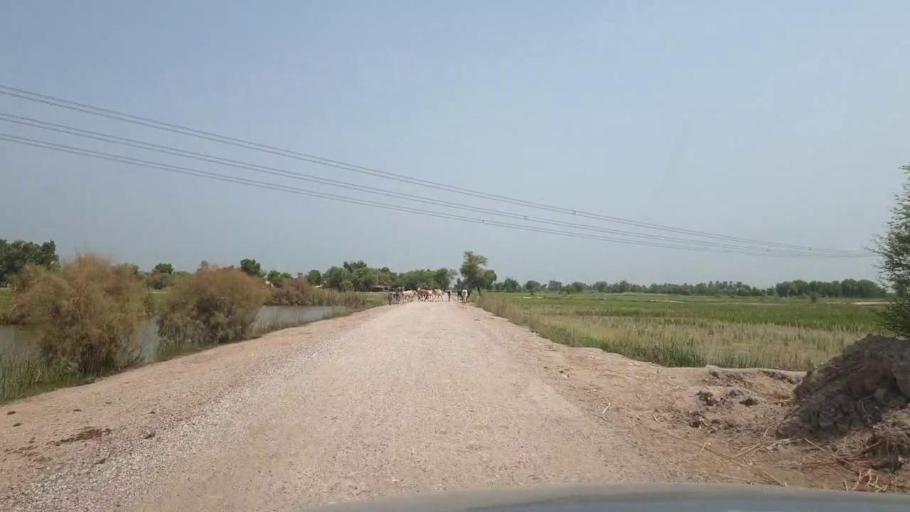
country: PK
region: Sindh
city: Madeji
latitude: 27.8054
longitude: 68.5203
